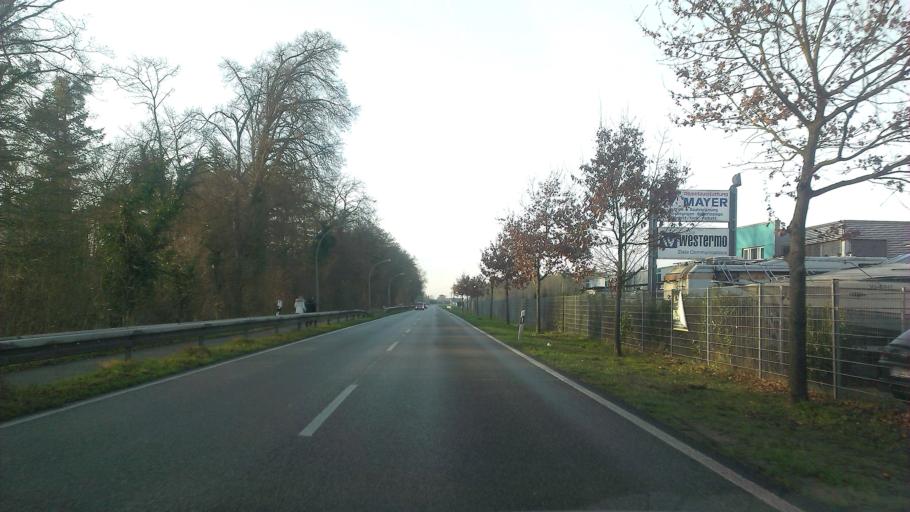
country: DE
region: Baden-Wuerttemberg
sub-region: Karlsruhe Region
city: Waghausel
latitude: 49.2471
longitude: 8.5306
